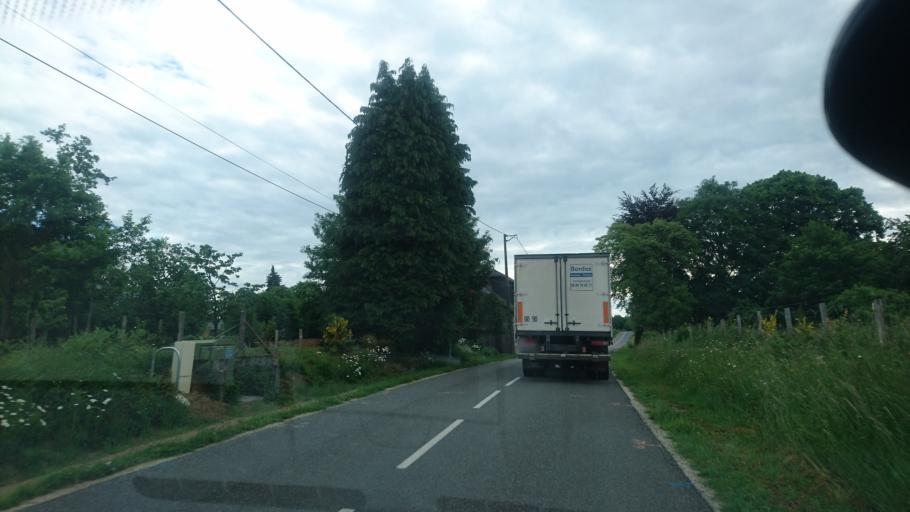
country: FR
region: Limousin
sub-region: Departement de la Haute-Vienne
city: Linards
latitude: 45.6553
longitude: 1.5503
